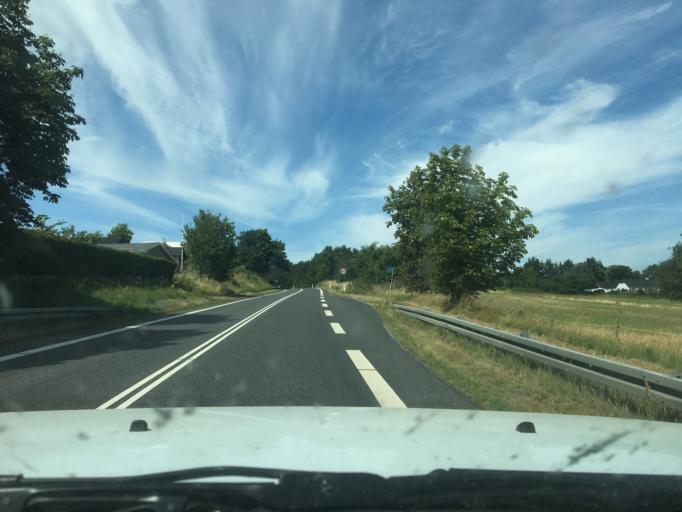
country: DK
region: Central Jutland
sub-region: Viborg Kommune
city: Viborg
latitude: 56.5756
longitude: 9.3775
